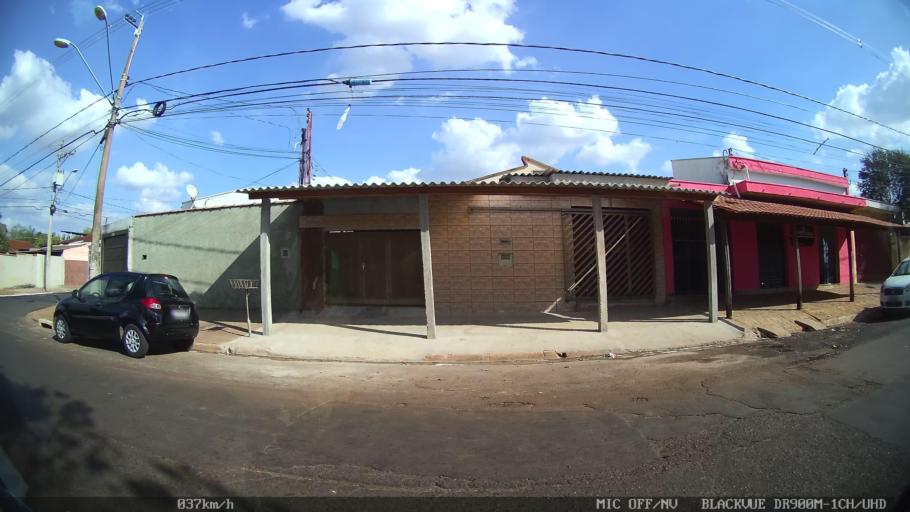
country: BR
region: Sao Paulo
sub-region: Ribeirao Preto
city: Ribeirao Preto
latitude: -21.1869
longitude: -47.8362
